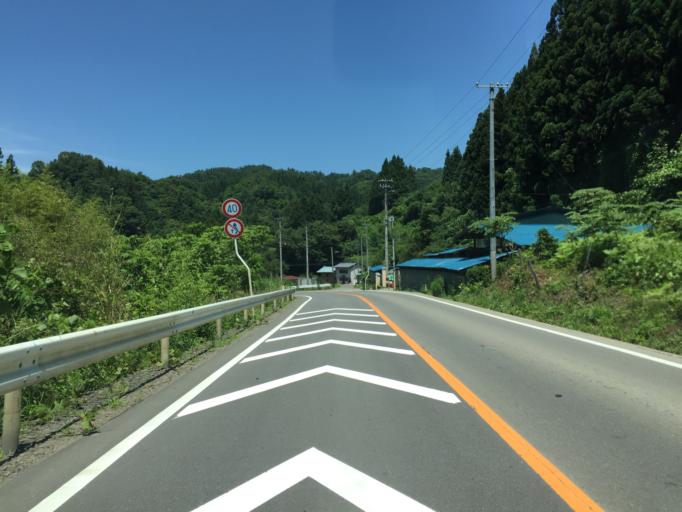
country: JP
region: Fukushima
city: Yanagawamachi-saiwaicho
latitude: 37.7584
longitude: 140.6624
